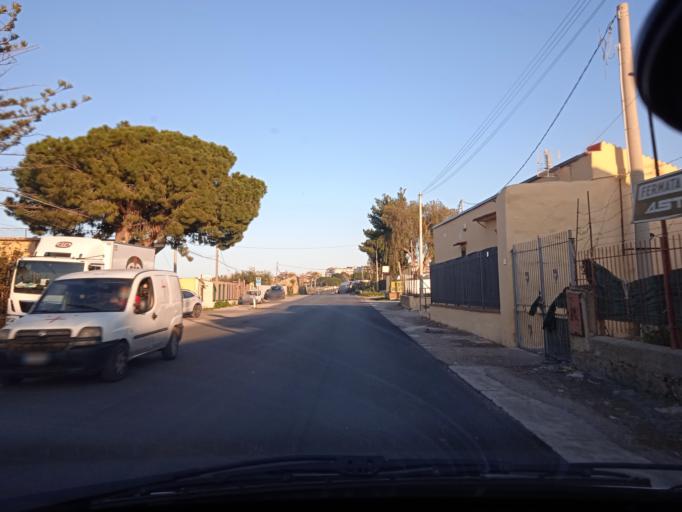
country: IT
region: Sicily
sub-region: Palermo
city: Bagheria
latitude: 38.0894
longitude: 13.4920
